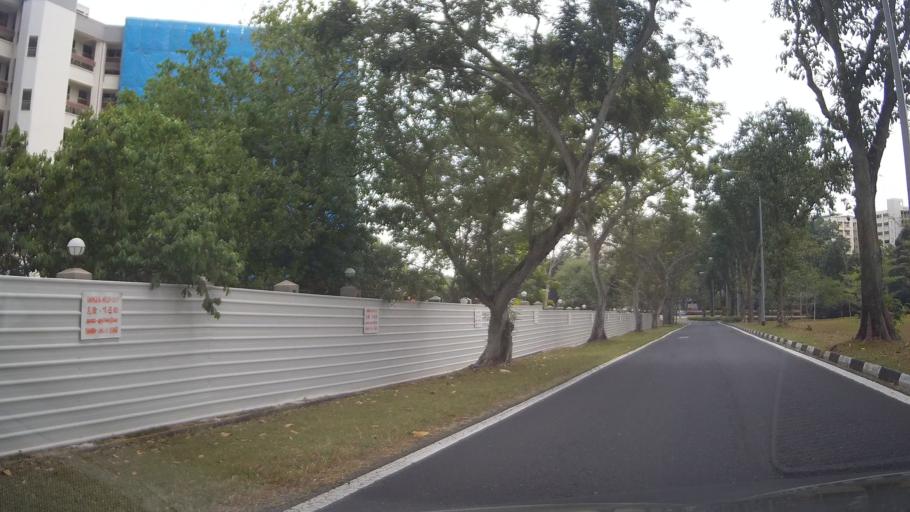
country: SG
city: Singapore
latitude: 1.3438
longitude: 103.9476
